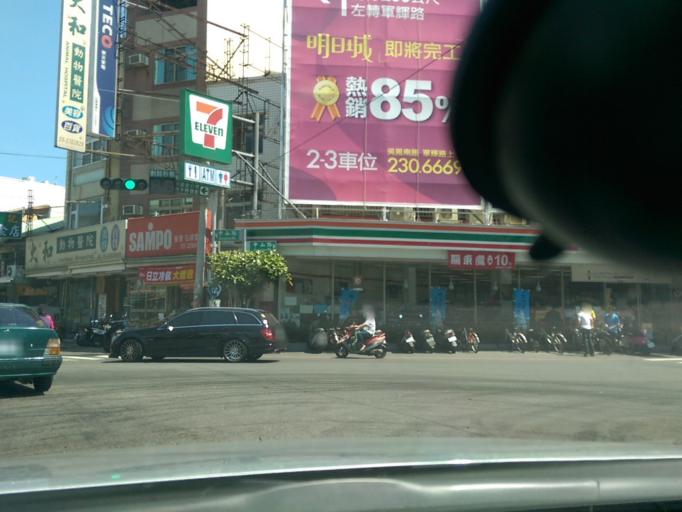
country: TW
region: Taiwan
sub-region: Chiayi
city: Jiayi Shi
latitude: 23.4518
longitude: 120.4606
